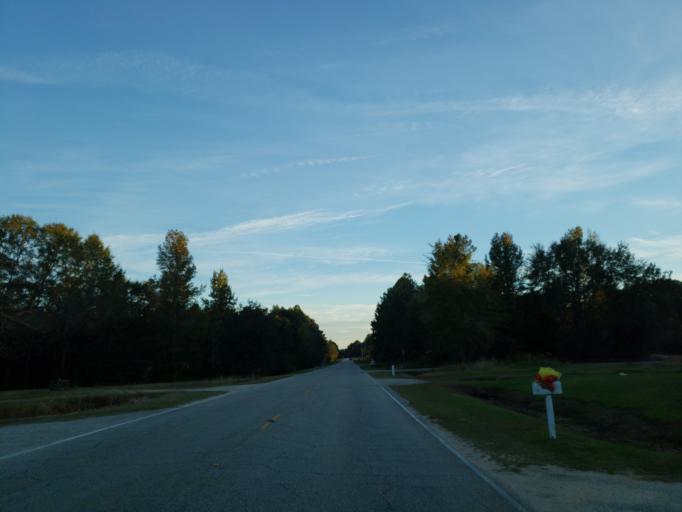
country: US
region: Mississippi
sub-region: Wayne County
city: Belmont
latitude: 31.4212
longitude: -88.4708
